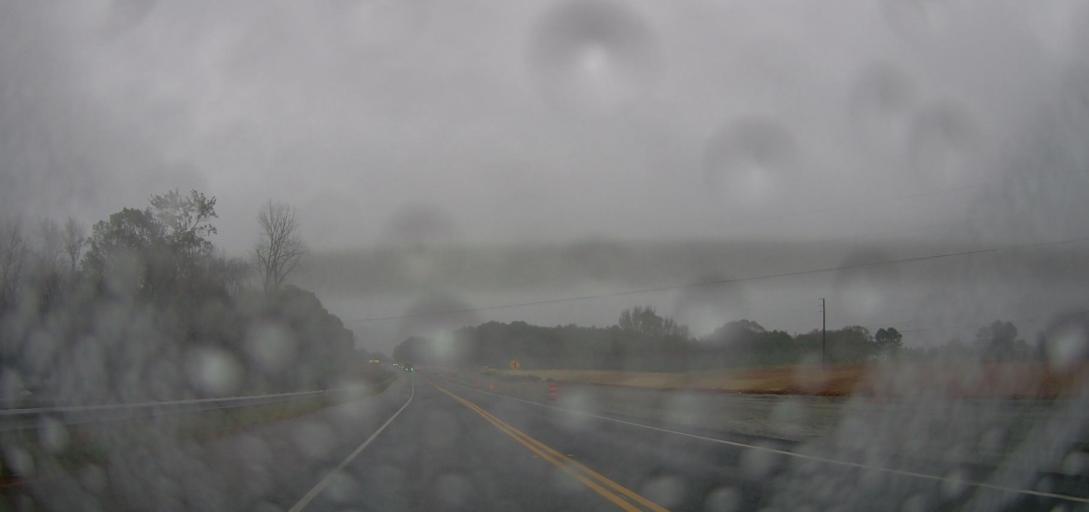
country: US
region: Georgia
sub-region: Morgan County
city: Madison
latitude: 33.5349
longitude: -83.4551
